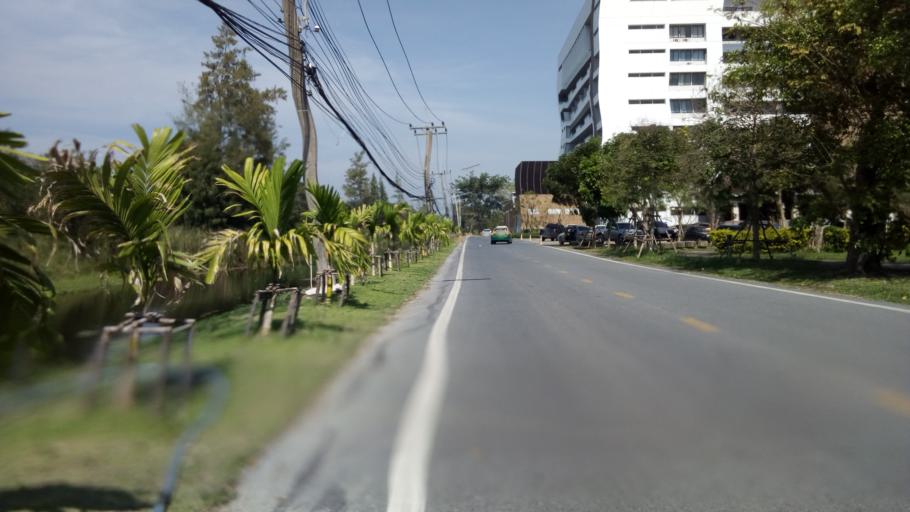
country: TH
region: Pathum Thani
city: Nong Suea
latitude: 14.0675
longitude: 100.8362
